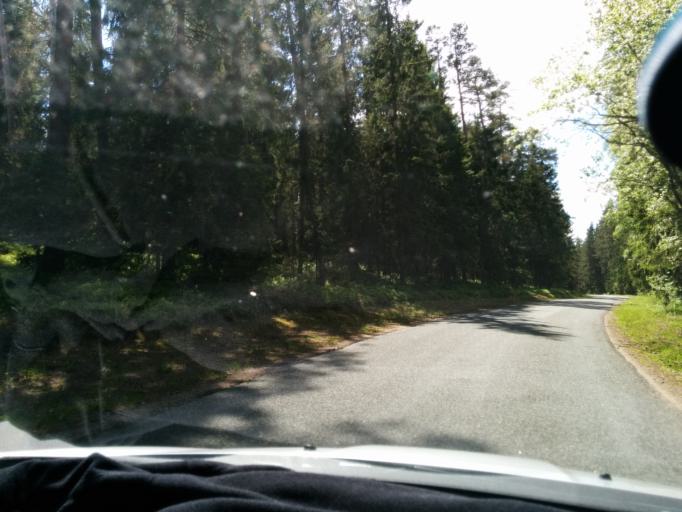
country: EE
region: Laeaene-Virumaa
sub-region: Kadrina vald
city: Kadrina
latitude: 59.5563
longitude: 25.9934
